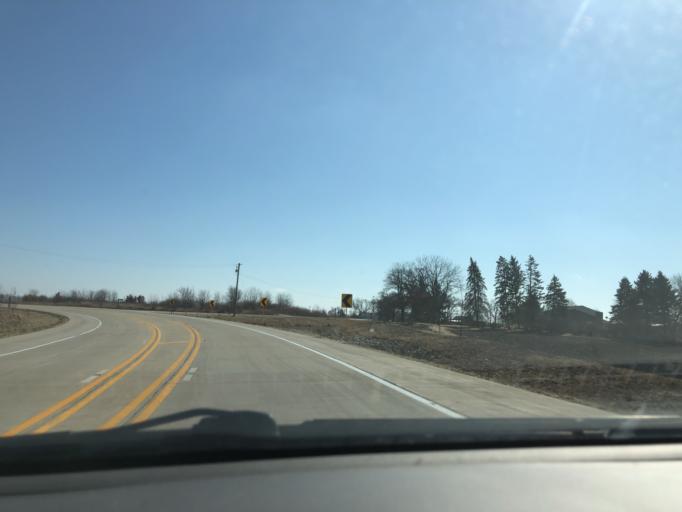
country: US
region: Illinois
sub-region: Kane County
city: Hampshire
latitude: 42.1022
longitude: -88.4847
